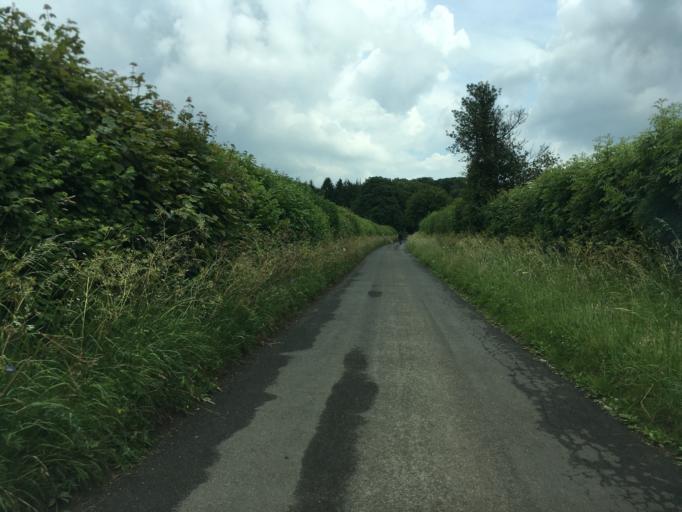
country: GB
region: England
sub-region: Gloucestershire
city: Shurdington
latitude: 51.8061
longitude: -2.0851
